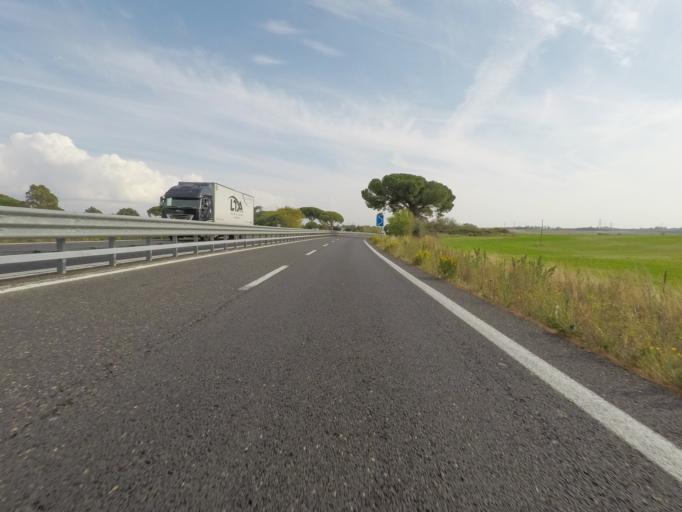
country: IT
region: Latium
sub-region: Provincia di Viterbo
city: Pescia Romana
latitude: 42.3902
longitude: 11.5411
